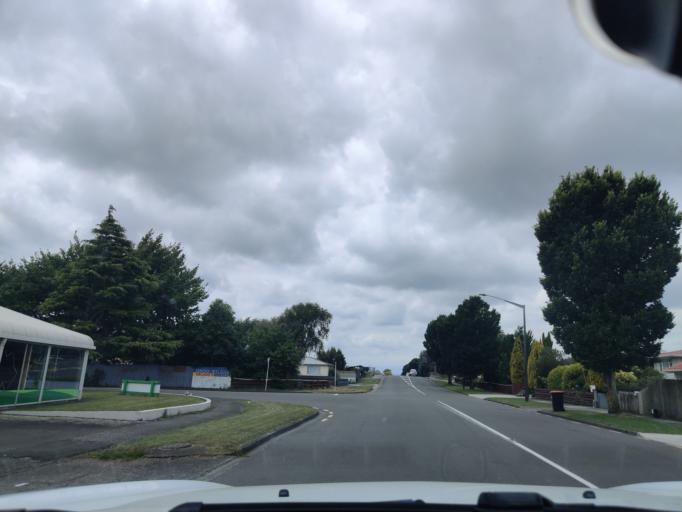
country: NZ
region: Manawatu-Wanganui
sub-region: Palmerston North City
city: Palmerston North
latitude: -40.3493
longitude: 175.5883
